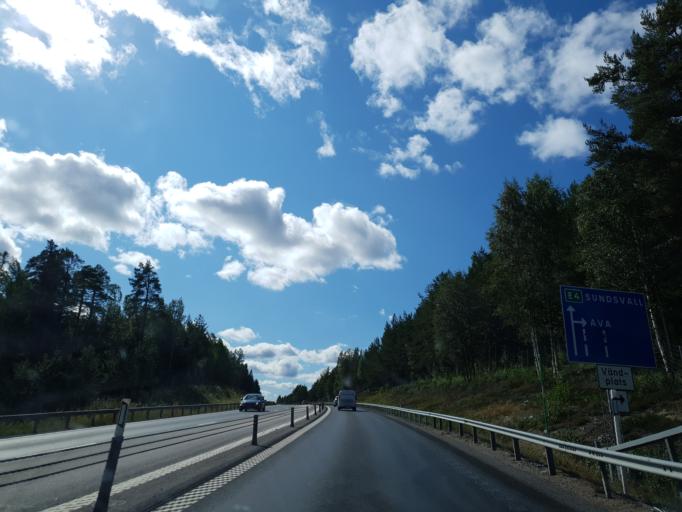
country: SE
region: Vaesterbotten
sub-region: Nordmalings Kommun
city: Nordmaling
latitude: 63.4974
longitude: 19.3247
